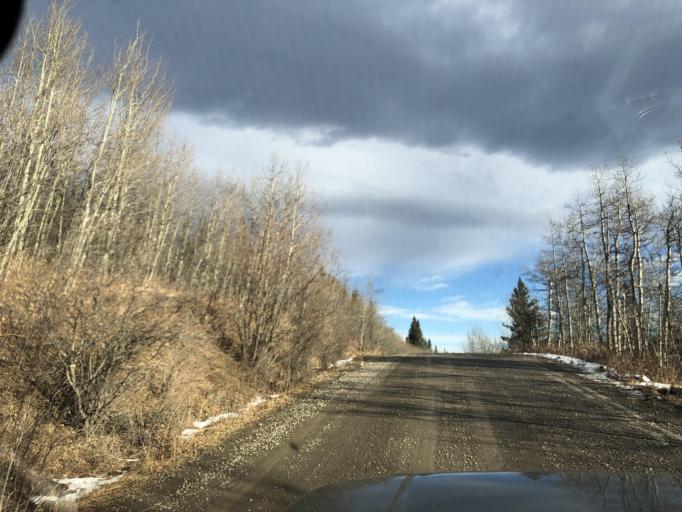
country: CA
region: Alberta
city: Cochrane
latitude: 51.0231
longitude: -114.8956
